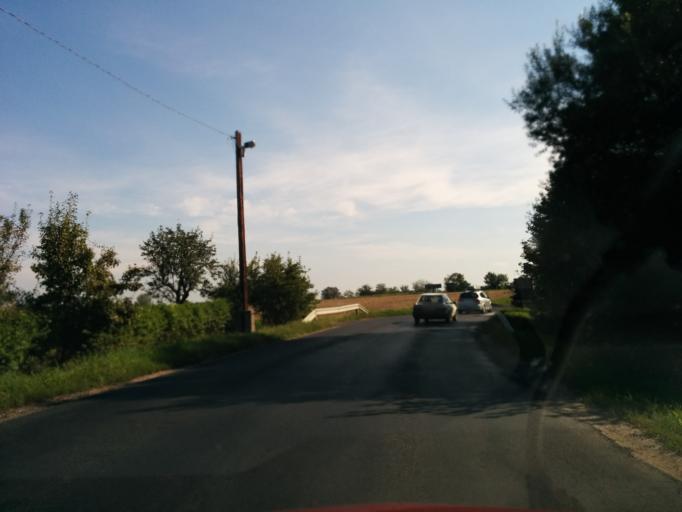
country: HU
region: Gyor-Moson-Sopron
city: Fertoszentmiklos
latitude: 47.5572
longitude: 16.8384
